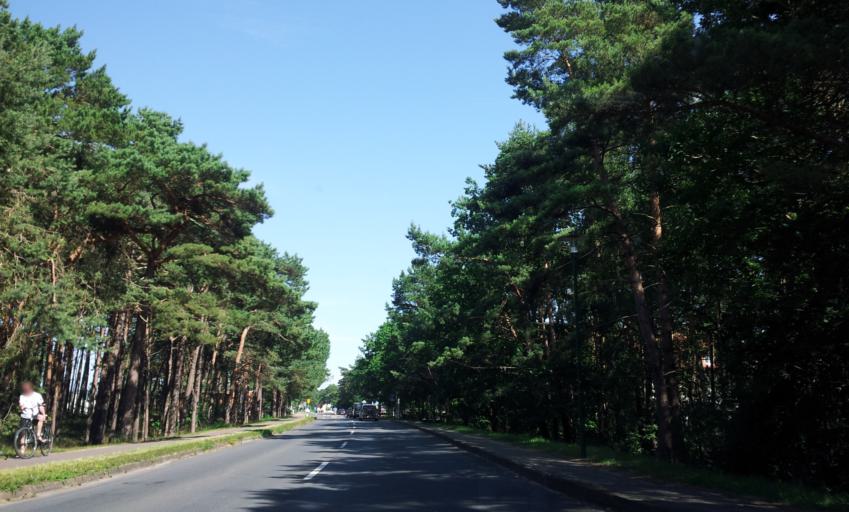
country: DE
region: Mecklenburg-Vorpommern
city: Glowe
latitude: 54.5691
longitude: 13.4554
